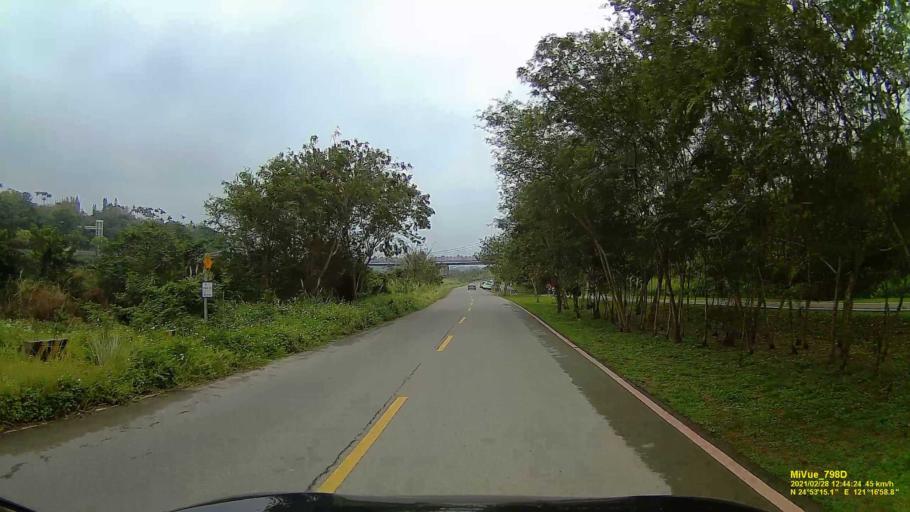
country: TW
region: Taiwan
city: Daxi
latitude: 24.8875
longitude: 121.2830
